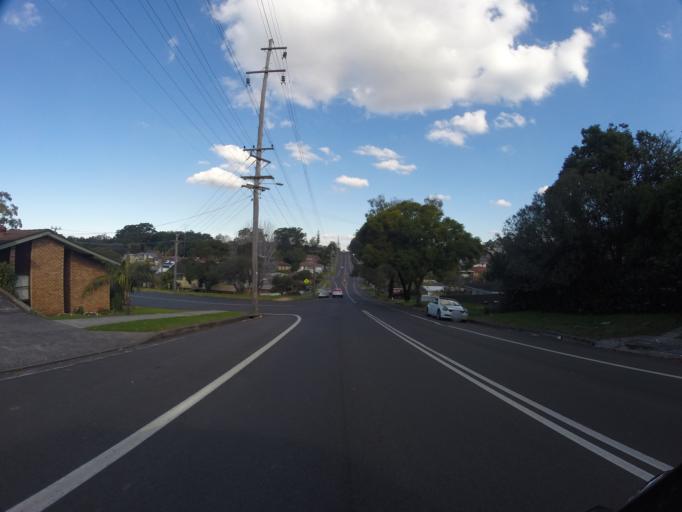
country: AU
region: New South Wales
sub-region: Wollongong
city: Keiraville
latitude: -34.4171
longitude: 150.8698
